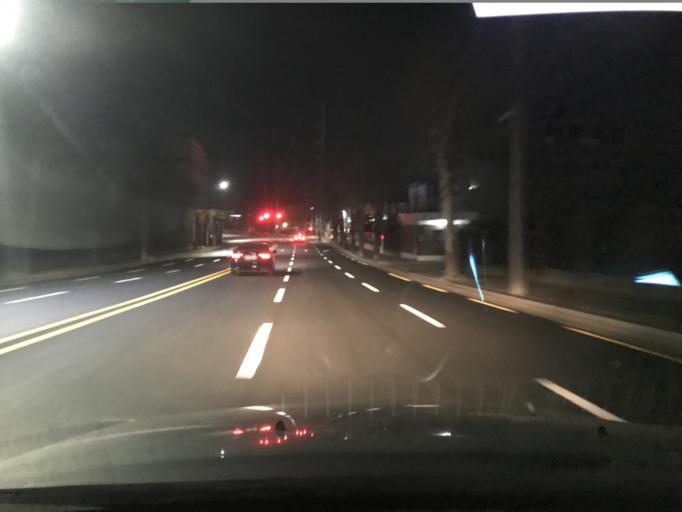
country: KR
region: Daegu
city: Hwawon
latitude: 35.7301
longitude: 128.4631
